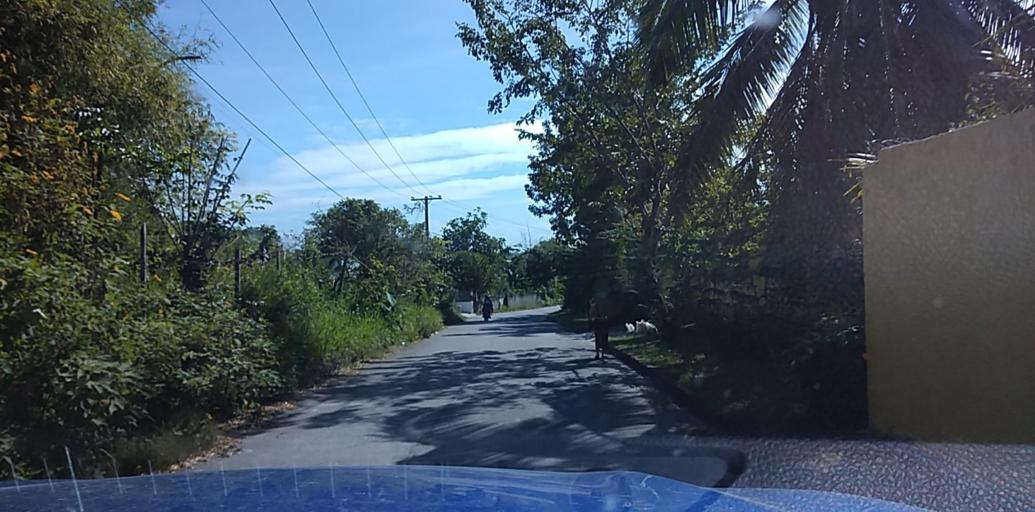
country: PH
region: Central Luzon
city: Santol
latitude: 15.1692
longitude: 120.4991
